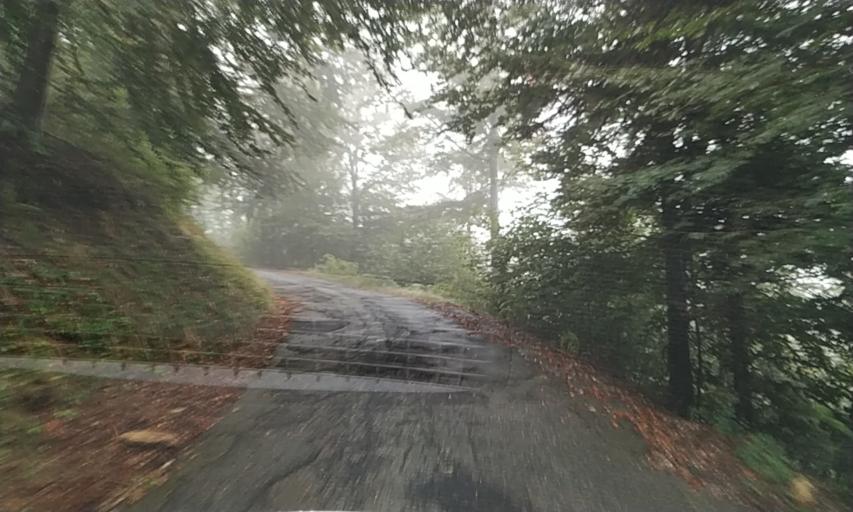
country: IT
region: Piedmont
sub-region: Provincia di Vercelli
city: Civiasco
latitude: 45.8336
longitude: 8.2957
